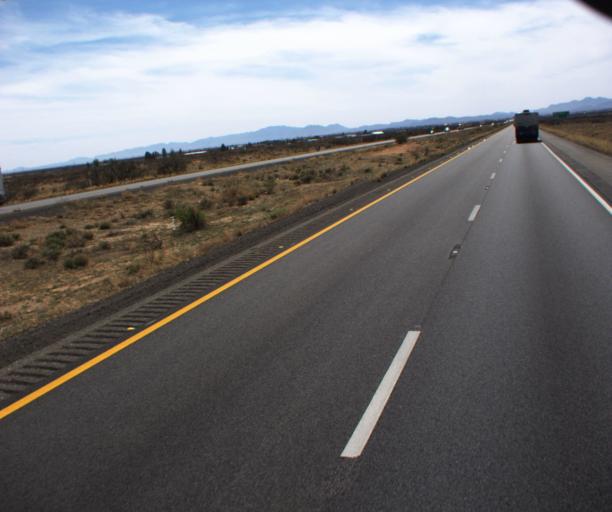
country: US
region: Arizona
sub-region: Cochise County
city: Willcox
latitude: 32.3038
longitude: -109.8017
